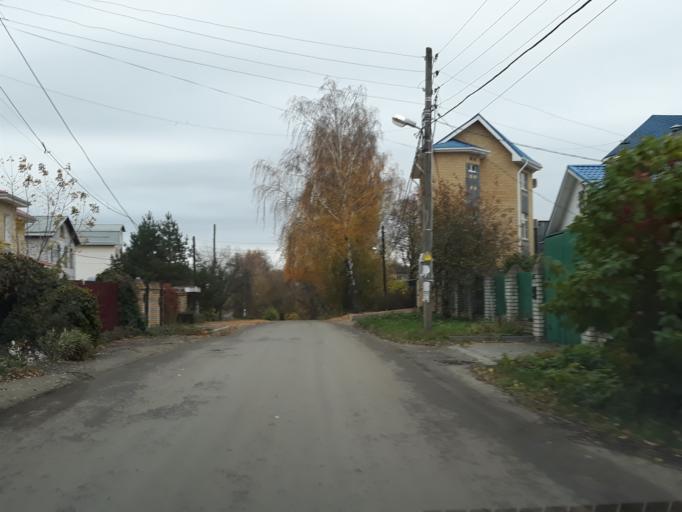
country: RU
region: Nizjnij Novgorod
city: Nizhniy Novgorod
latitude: 56.2540
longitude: 43.9743
